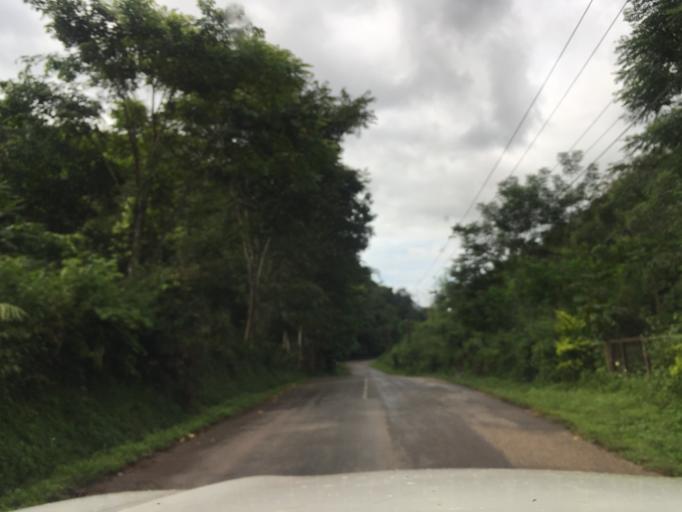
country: LA
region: Oudomxai
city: Muang La
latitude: 20.8041
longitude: 102.0878
